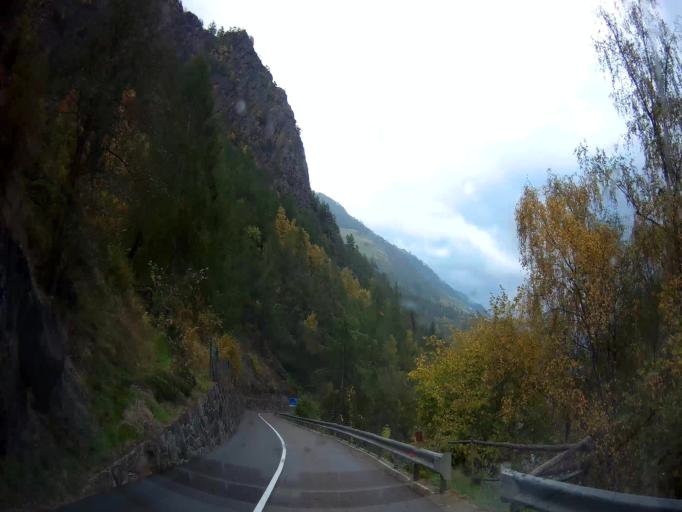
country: IT
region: Trentino-Alto Adige
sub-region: Bolzano
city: Certosa
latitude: 46.7010
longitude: 10.9203
